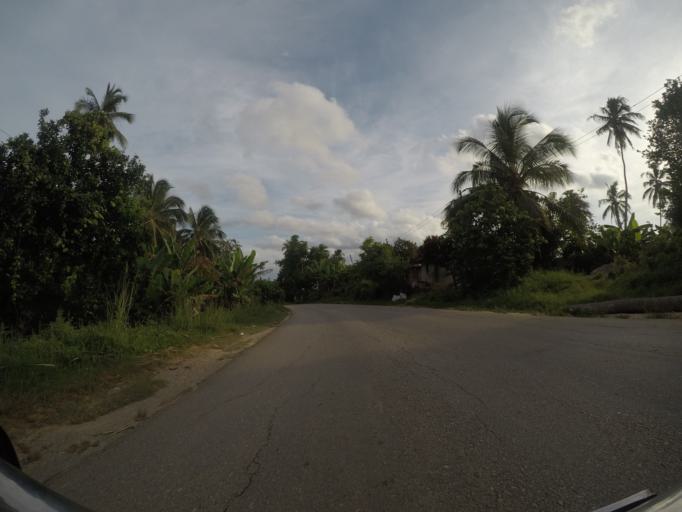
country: TZ
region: Pemba South
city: Chake Chake
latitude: -5.2642
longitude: 39.7719
